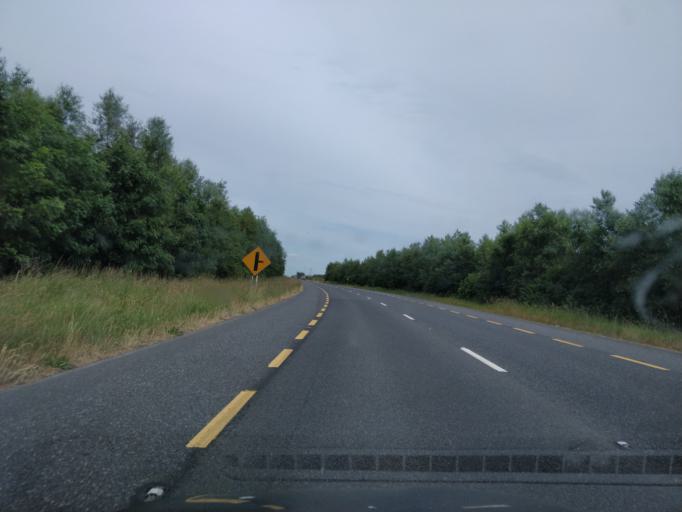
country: IE
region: Leinster
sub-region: Uibh Fhaili
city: Tullamore
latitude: 53.2518
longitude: -7.4876
